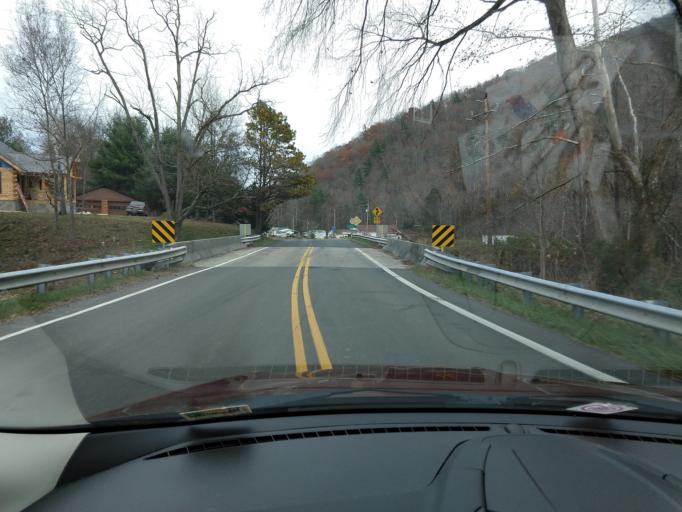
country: US
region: West Virginia
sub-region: Greenbrier County
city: White Sulphur Springs
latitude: 37.7195
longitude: -80.2009
